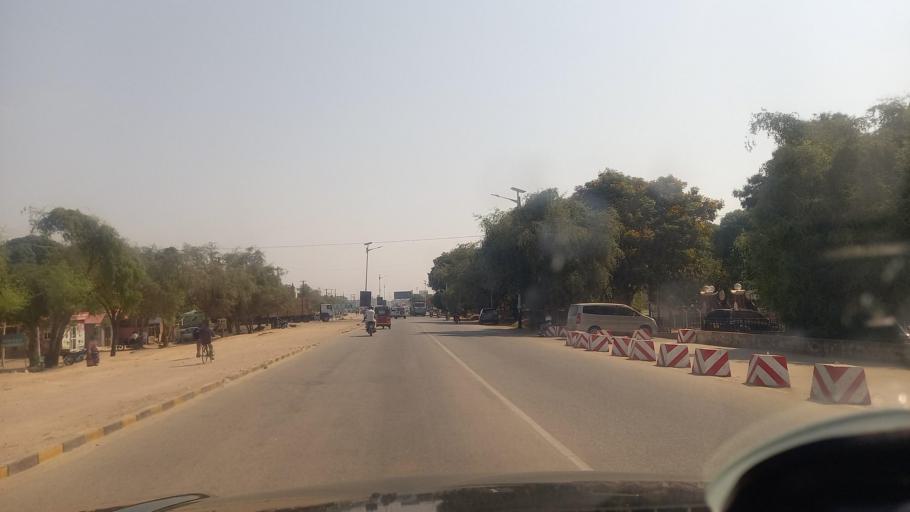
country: TZ
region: Dodoma
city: Dodoma
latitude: -6.1787
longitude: 35.7570
